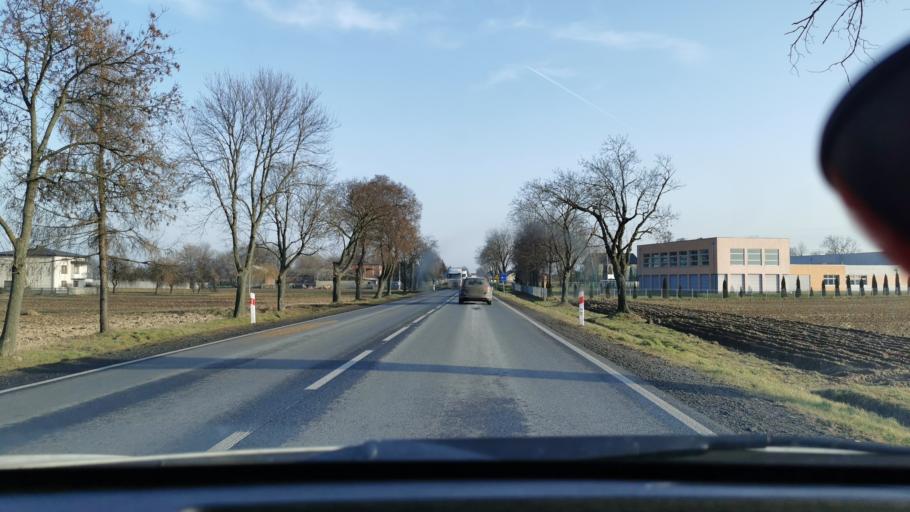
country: PL
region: Lodz Voivodeship
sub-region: Powiat sieradzki
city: Wroblew
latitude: 51.6323
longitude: 18.5439
